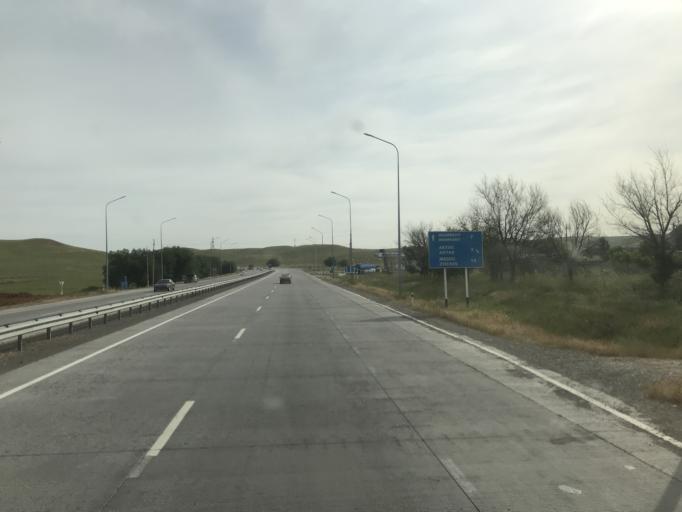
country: KZ
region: Ongtustik Qazaqstan
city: Shymkent
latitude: 42.2172
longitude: 69.5274
